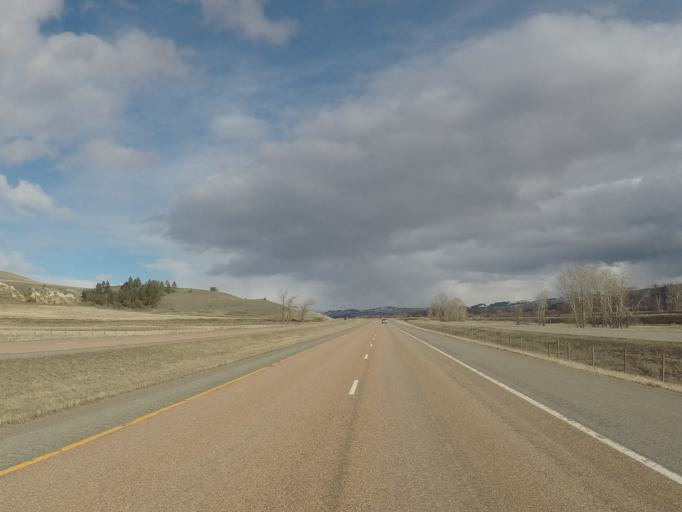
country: US
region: Montana
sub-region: Granite County
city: Philipsburg
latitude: 46.6345
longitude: -113.0934
